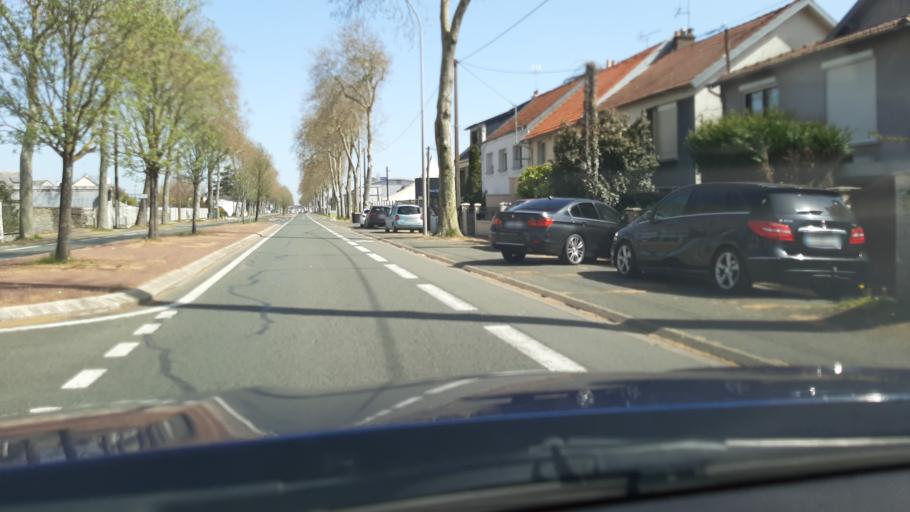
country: FR
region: Pays de la Loire
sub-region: Departement de Maine-et-Loire
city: Angers
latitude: 47.4874
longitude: -0.5120
